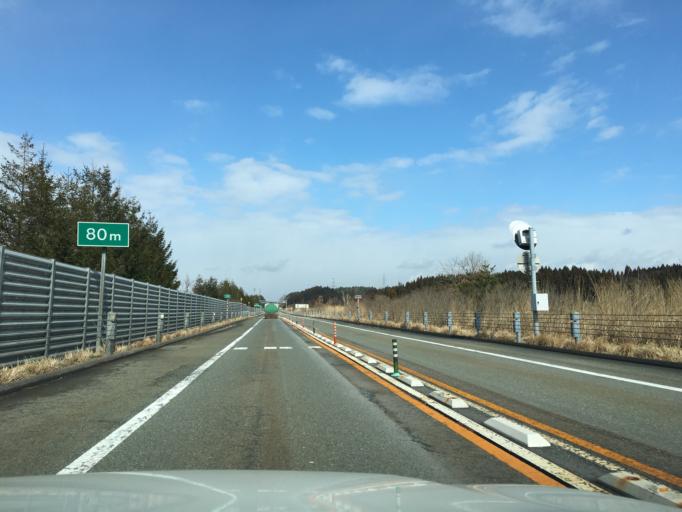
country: JP
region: Akita
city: Akita Shi
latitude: 39.7974
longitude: 140.1000
